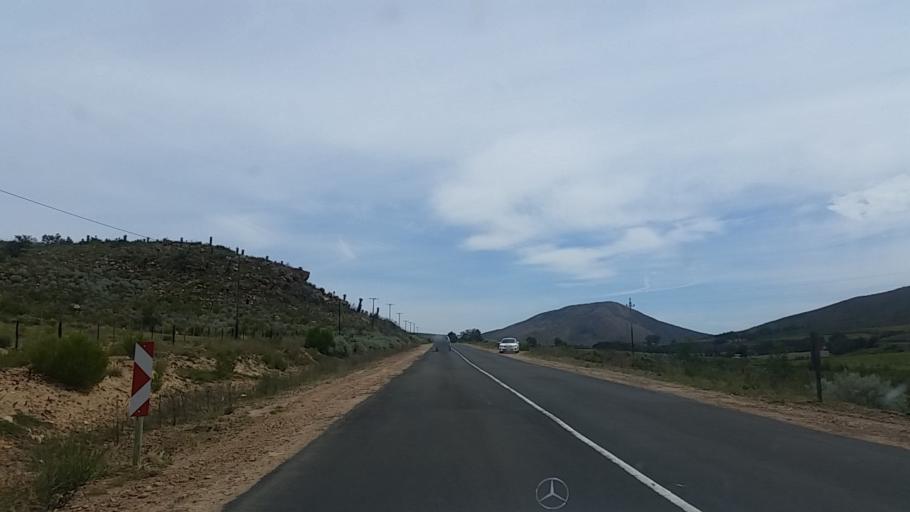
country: ZA
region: Western Cape
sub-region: Eden District Municipality
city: George
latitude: -33.8200
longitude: 22.3719
